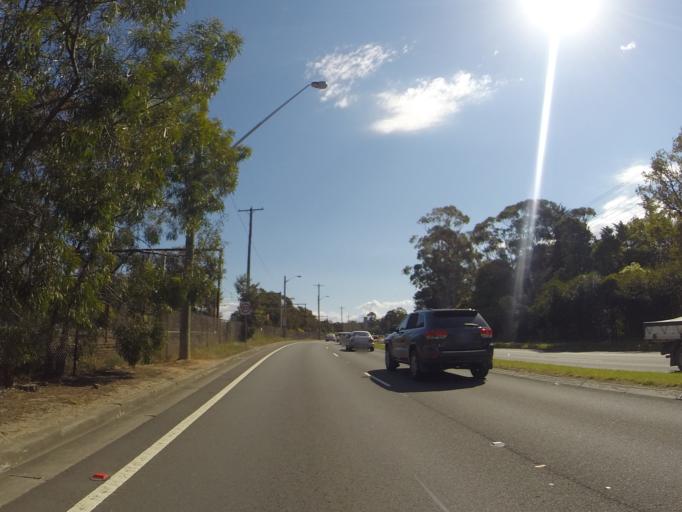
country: AU
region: New South Wales
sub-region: Blue Mountains Municipality
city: Blaxland
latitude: -33.6993
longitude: 150.5546
